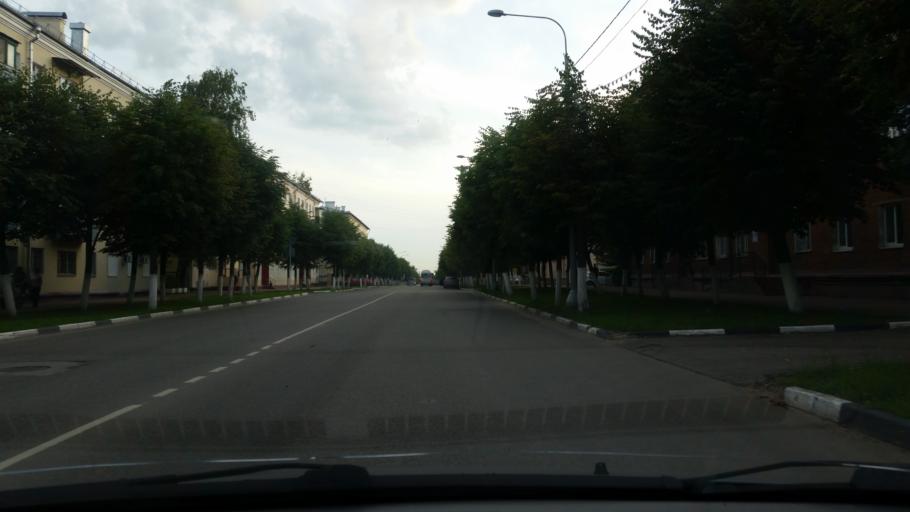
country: RU
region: Moskovskaya
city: Serpukhov
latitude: 54.9237
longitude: 37.4324
